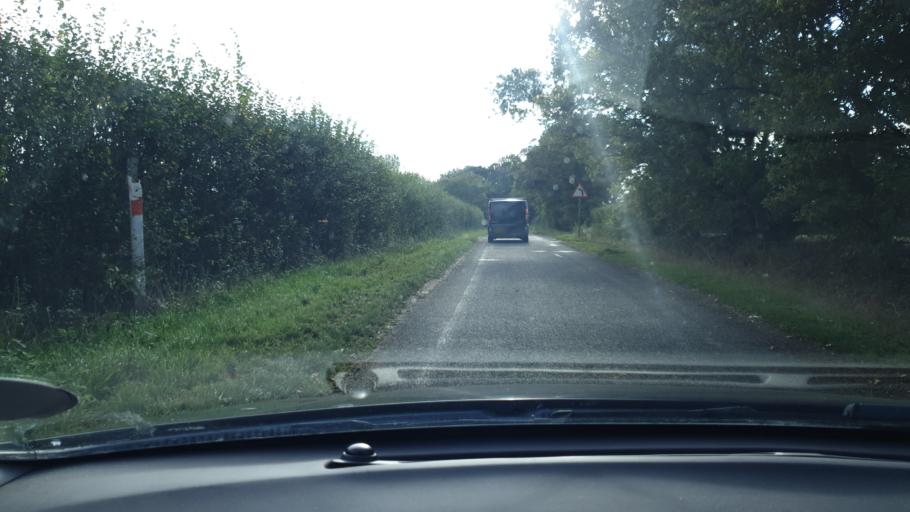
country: GB
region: England
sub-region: Essex
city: Alresford
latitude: 51.8617
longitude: 1.0193
